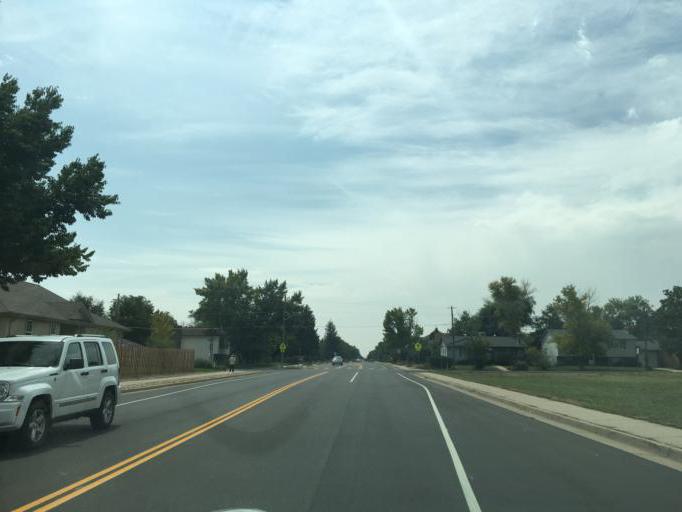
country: US
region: Colorado
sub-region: Adams County
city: Aurora
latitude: 39.7344
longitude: -104.8007
